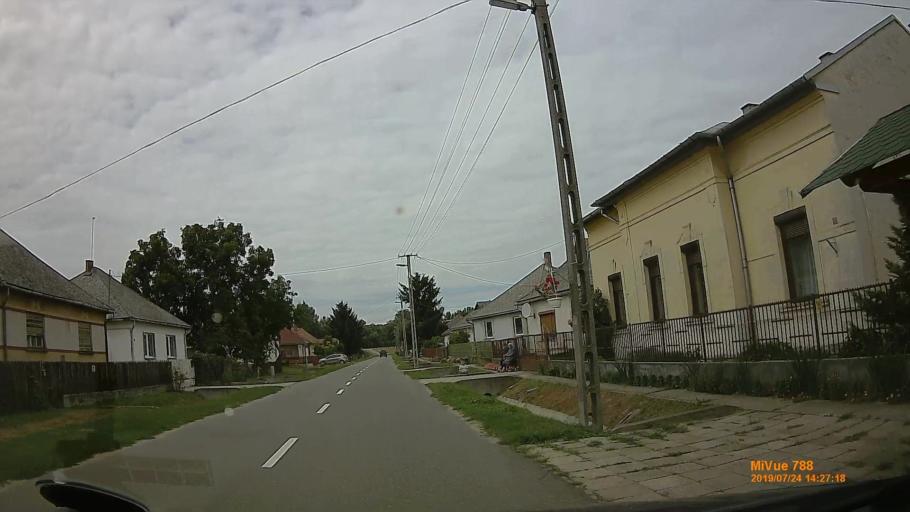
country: HU
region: Szabolcs-Szatmar-Bereg
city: Mandok
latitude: 48.3320
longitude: 22.2645
